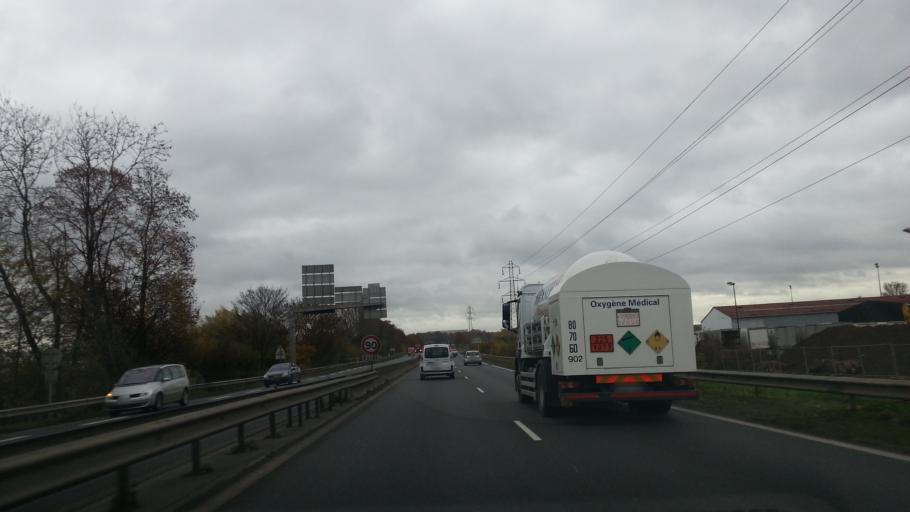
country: FR
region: Picardie
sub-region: Departement de l'Oise
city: Villers-Saint-Paul
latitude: 49.2817
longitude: 2.4789
